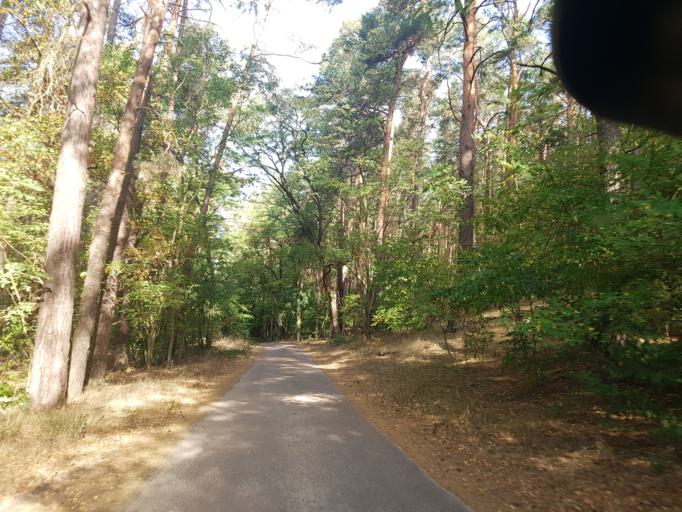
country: DE
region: Brandenburg
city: Belzig
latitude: 52.1509
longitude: 12.5798
